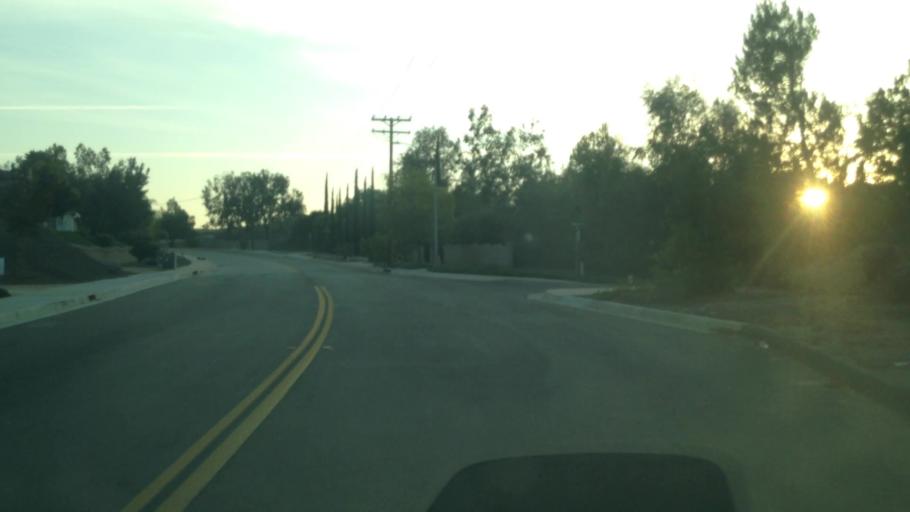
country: US
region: California
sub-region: Riverside County
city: Woodcrest
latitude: 33.8776
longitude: -117.4353
